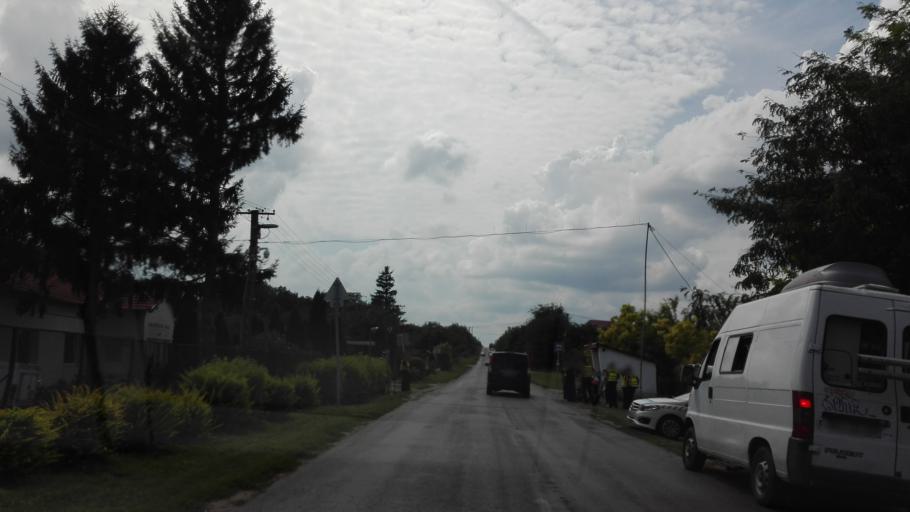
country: HU
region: Tolna
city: Simontornya
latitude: 46.7563
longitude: 18.5050
